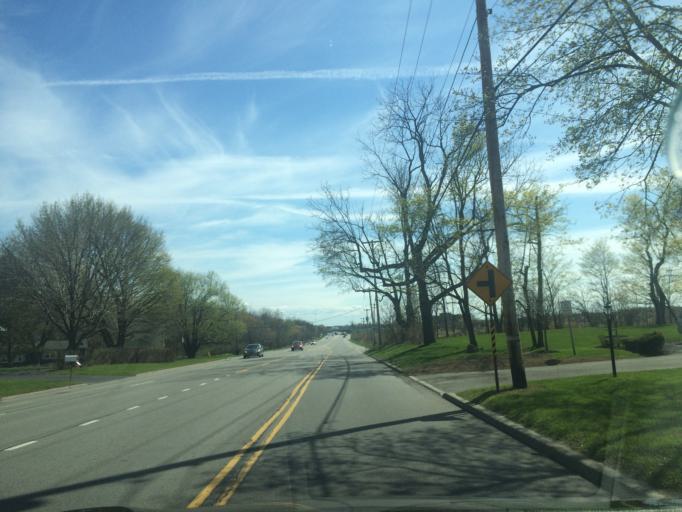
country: US
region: New York
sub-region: Monroe County
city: Brighton
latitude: 43.1157
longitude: -77.5716
